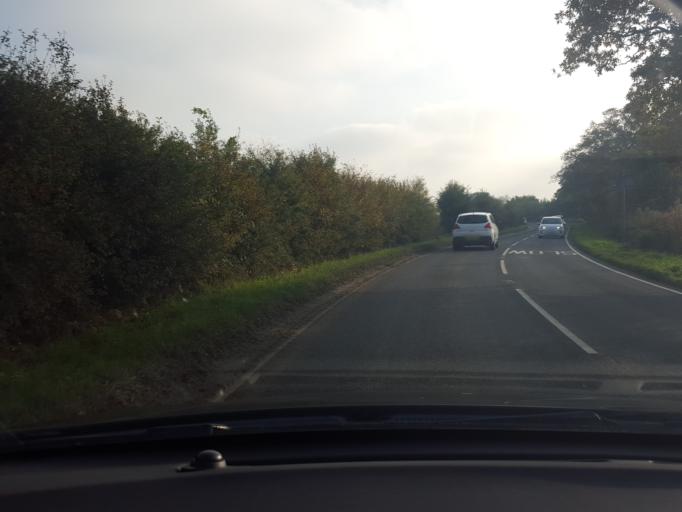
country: GB
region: England
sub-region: Essex
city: Little Clacton
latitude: 51.8681
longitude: 1.1750
